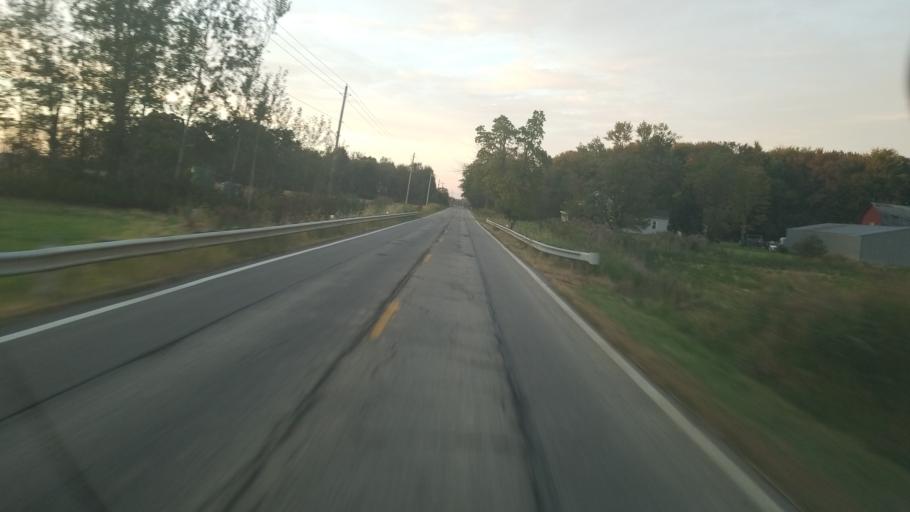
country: US
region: Ohio
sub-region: Ashtabula County
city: Andover
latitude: 41.6524
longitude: -80.6670
